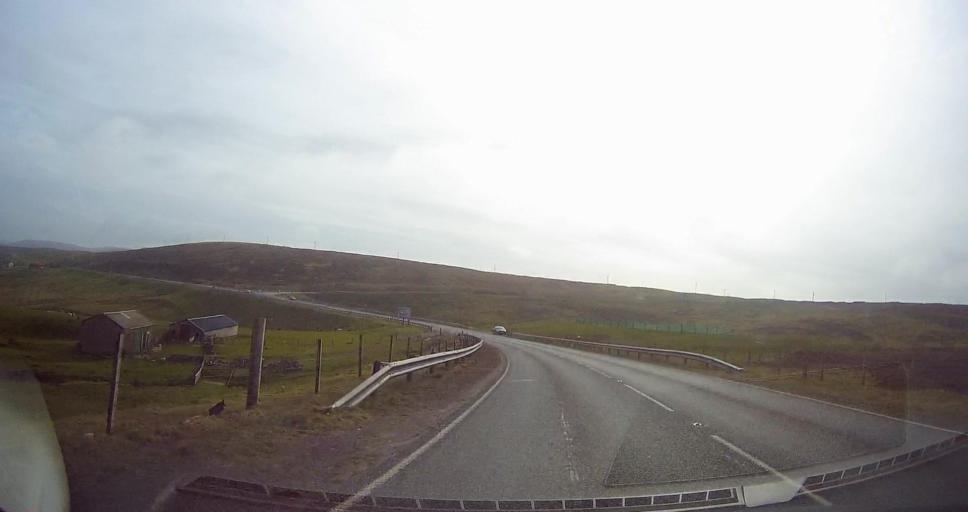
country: GB
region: Scotland
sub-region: Shetland Islands
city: Lerwick
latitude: 60.1391
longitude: -1.2085
